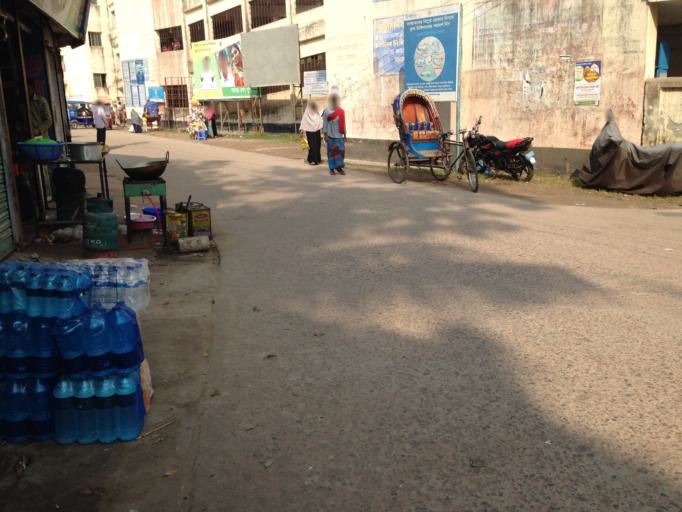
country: BD
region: Chittagong
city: Lakshmipur
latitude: 22.9341
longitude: 90.8326
